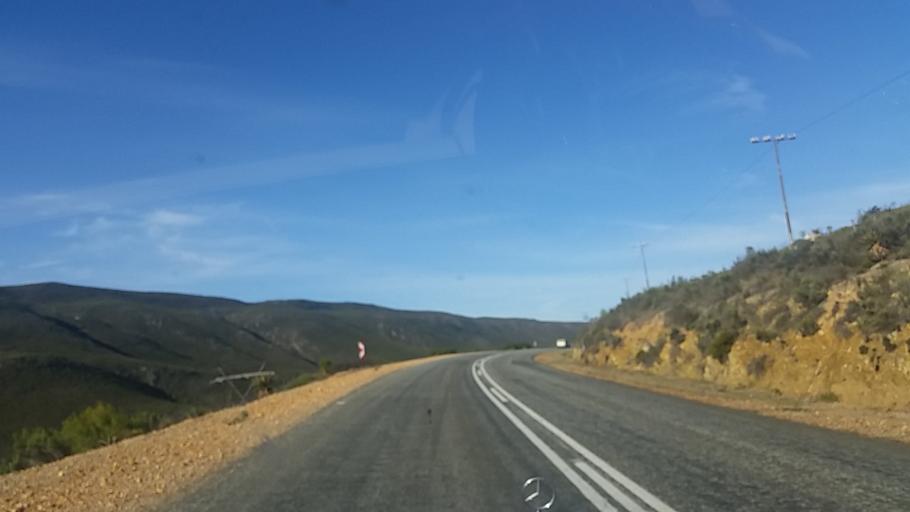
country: ZA
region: Western Cape
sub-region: Eden District Municipality
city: Knysna
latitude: -33.7472
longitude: 22.9810
